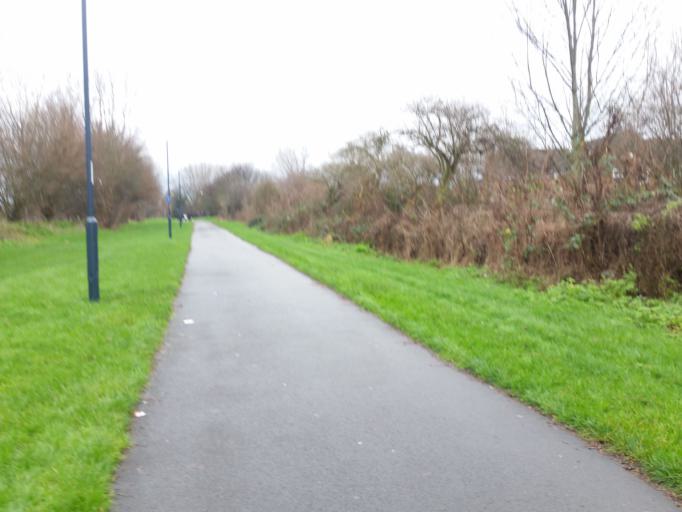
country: GB
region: England
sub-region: Derby
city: Derby
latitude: 52.8976
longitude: -1.4463
